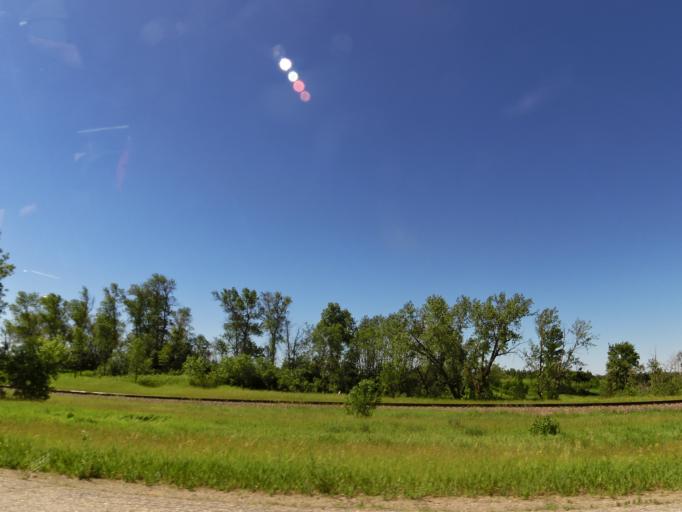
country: US
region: Minnesota
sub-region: Polk County
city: Fosston
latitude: 47.6626
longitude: -95.9924
